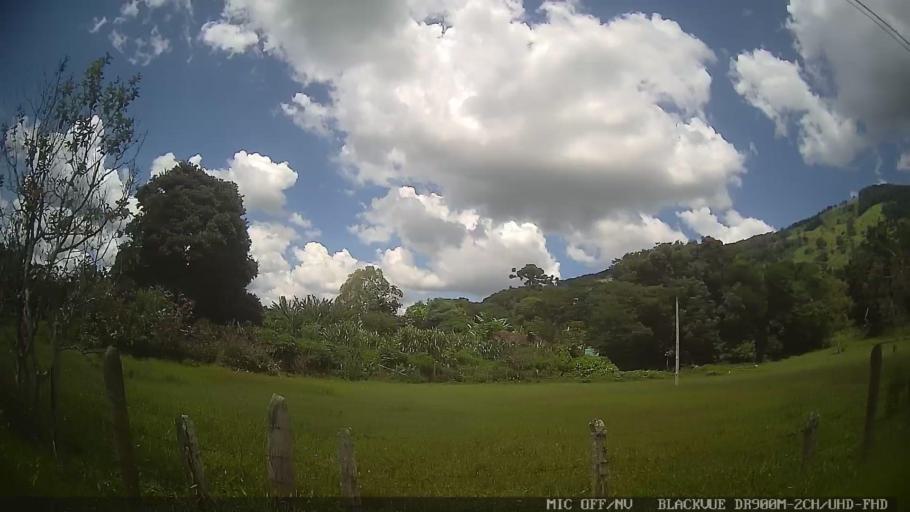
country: BR
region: Minas Gerais
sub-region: Extrema
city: Extrema
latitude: -22.8626
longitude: -46.2836
